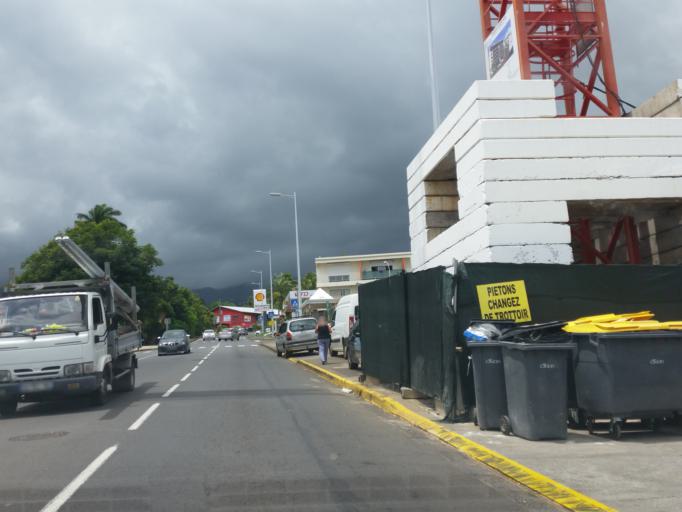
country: RE
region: Reunion
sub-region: Reunion
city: Saint-Denis
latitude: -20.9025
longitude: 55.4921
